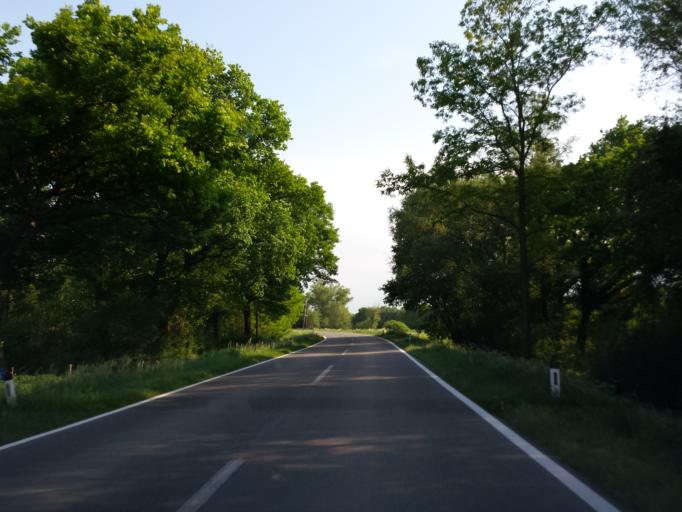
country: AT
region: Lower Austria
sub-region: Politischer Bezirk Ganserndorf
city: Marchegg
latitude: 48.2988
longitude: 16.8753
